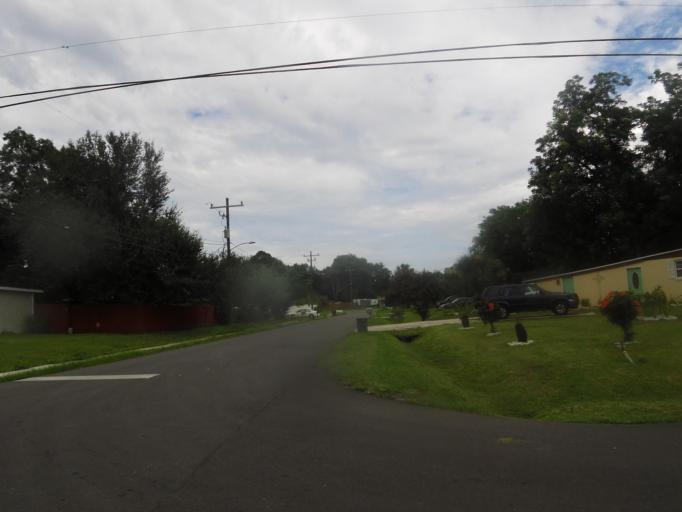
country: US
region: Florida
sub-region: Duval County
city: Jacksonville
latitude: 30.3170
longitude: -81.5311
